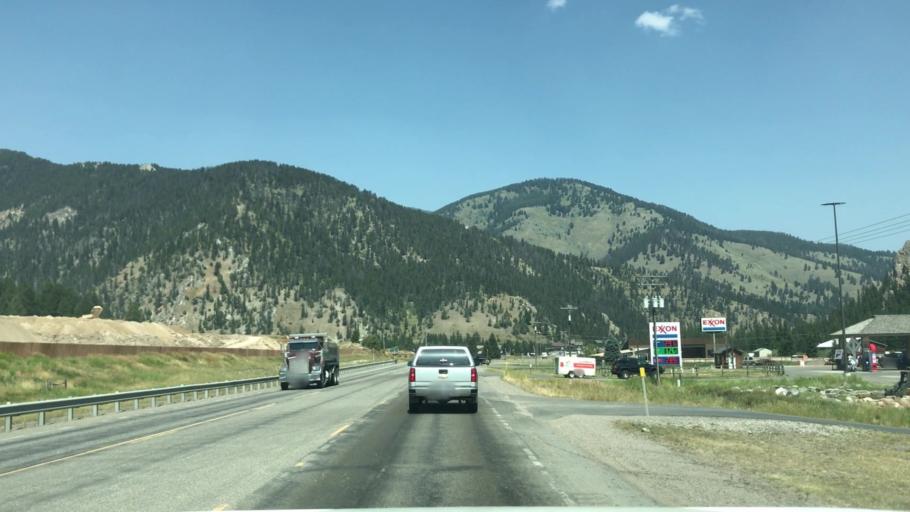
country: US
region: Montana
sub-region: Gallatin County
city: Big Sky
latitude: 45.2583
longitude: -111.2544
